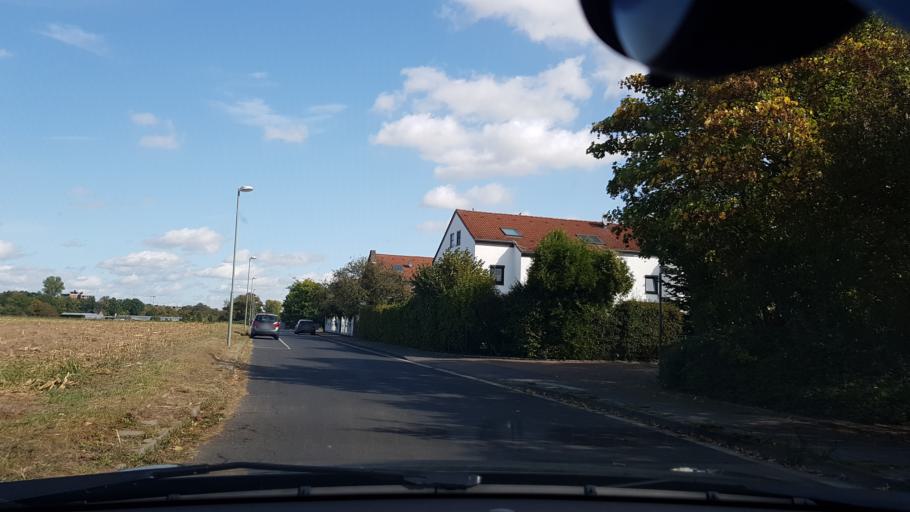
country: DE
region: North Rhine-Westphalia
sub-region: Regierungsbezirk Dusseldorf
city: Neuss
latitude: 51.1455
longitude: 6.6961
